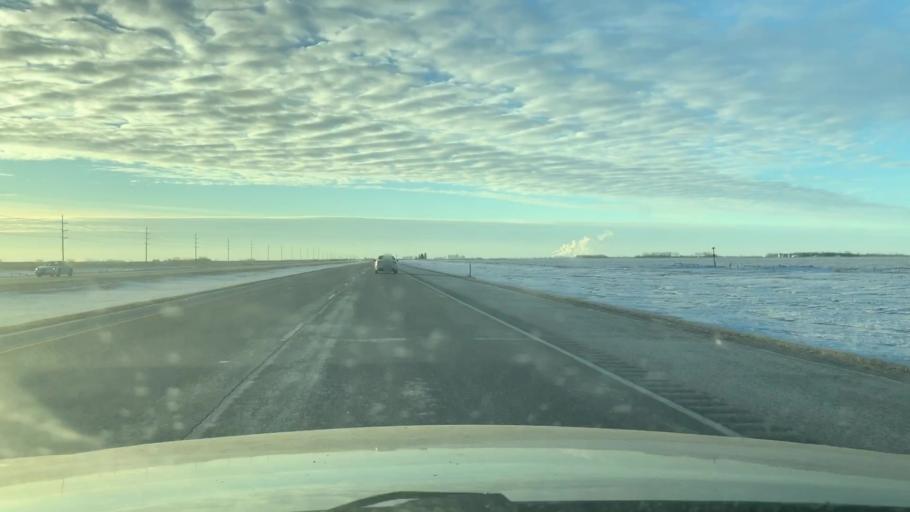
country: US
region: North Dakota
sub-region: Cass County
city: Casselton
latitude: 46.8768
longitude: -97.1146
